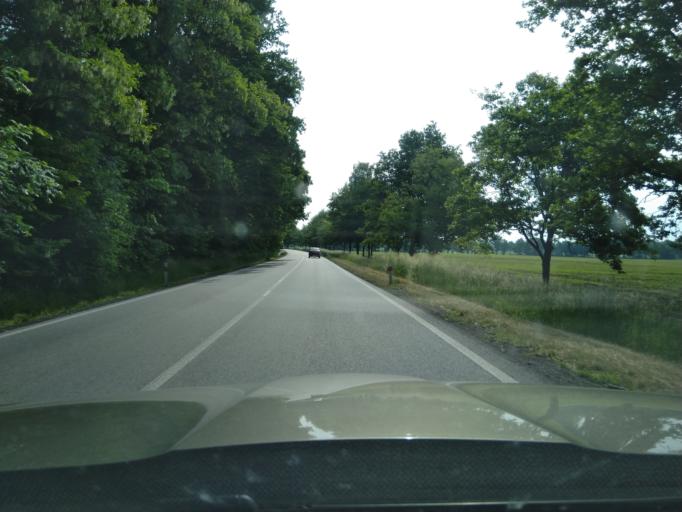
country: CZ
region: Jihocesky
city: Zliv
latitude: 49.0296
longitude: 14.2881
